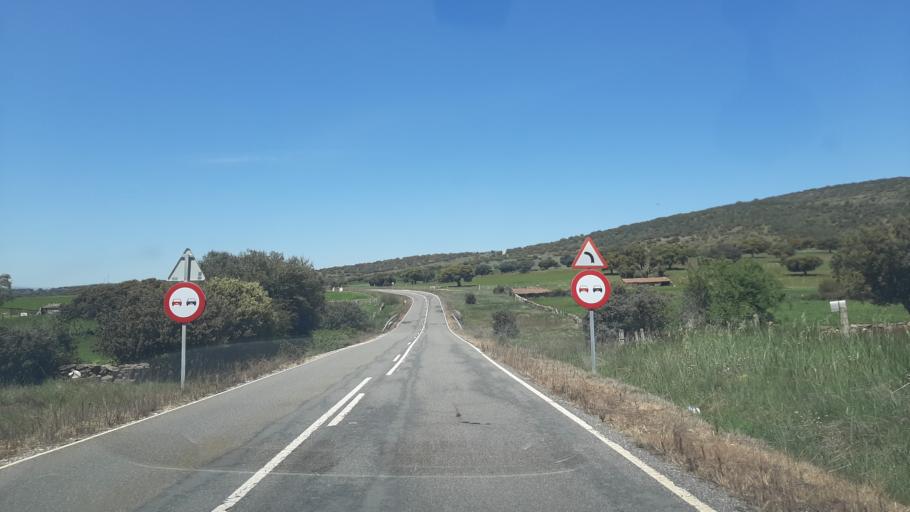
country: ES
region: Castille and Leon
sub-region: Provincia de Salamanca
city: Puente del Congosto
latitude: 40.5347
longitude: -5.5282
